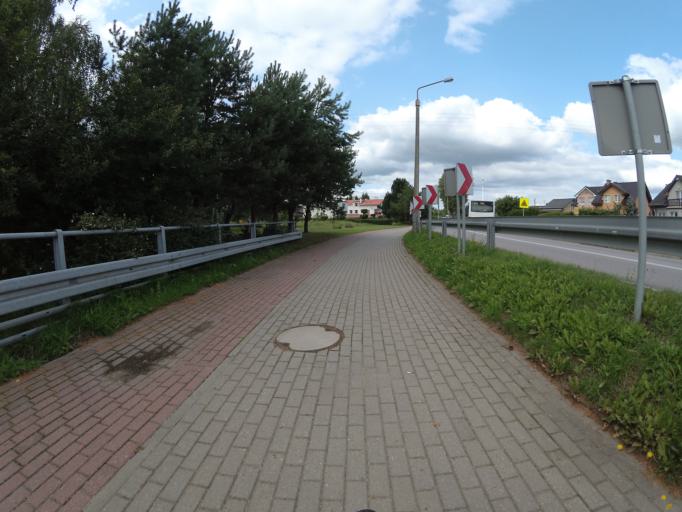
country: PL
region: Pomeranian Voivodeship
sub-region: Powiat wejherowski
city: Bojano
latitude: 54.4933
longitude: 18.4207
